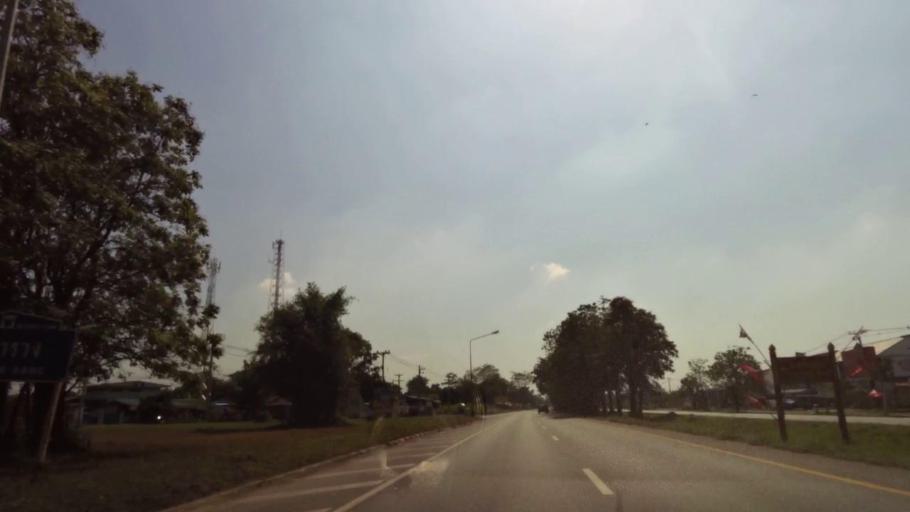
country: TH
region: Phichit
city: Bueng Na Rang
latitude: 16.1900
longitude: 100.1287
